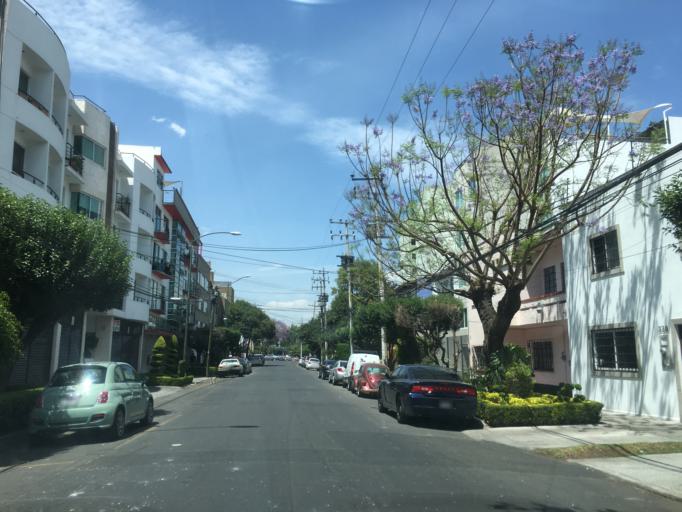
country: MX
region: Mexico City
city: Benito Juarez
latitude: 19.3974
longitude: -99.1602
